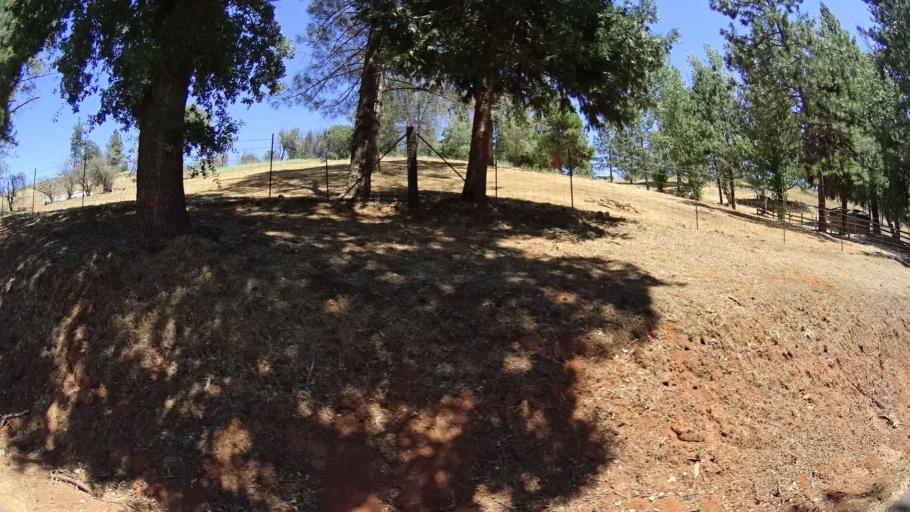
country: US
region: California
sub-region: Calaveras County
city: Mountain Ranch
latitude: 38.2775
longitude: -120.5070
